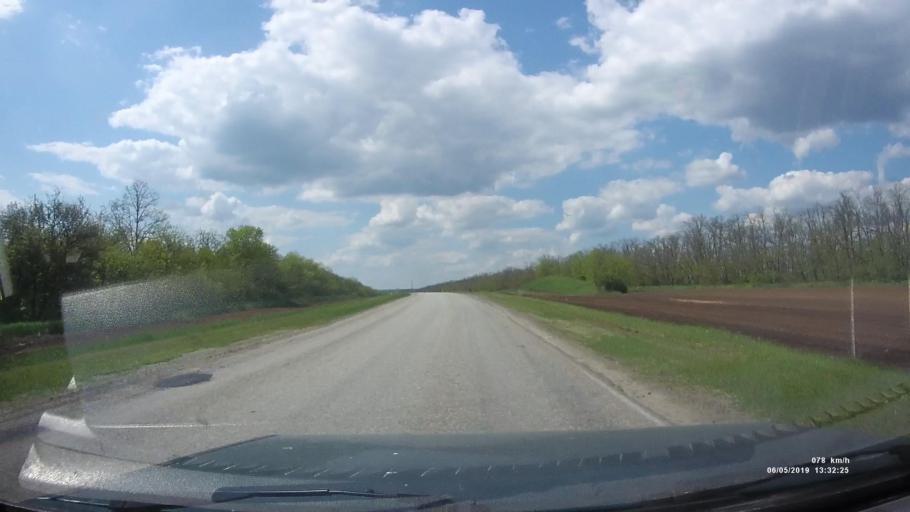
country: RU
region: Rostov
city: Ust'-Donetskiy
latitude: 47.6833
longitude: 40.7962
